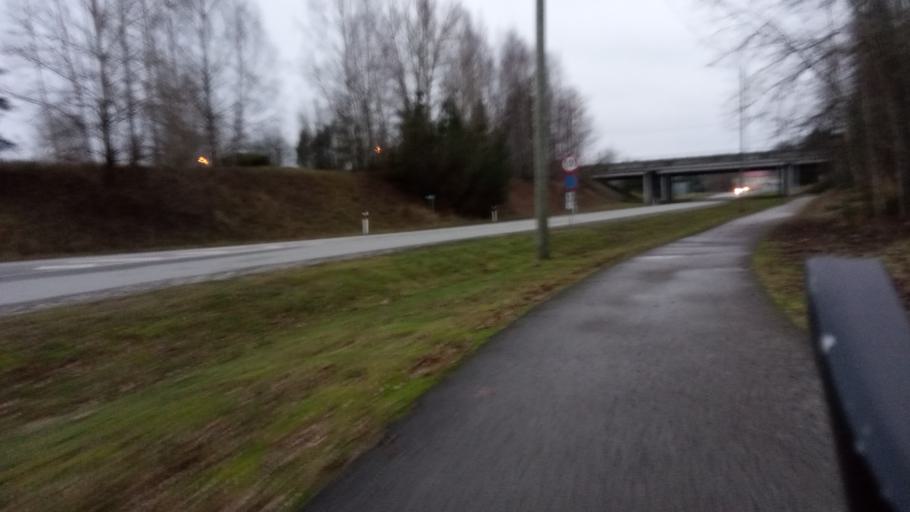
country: EE
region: Harju
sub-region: Kuusalu vald
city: Kuusalu
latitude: 59.4497
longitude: 25.4326
